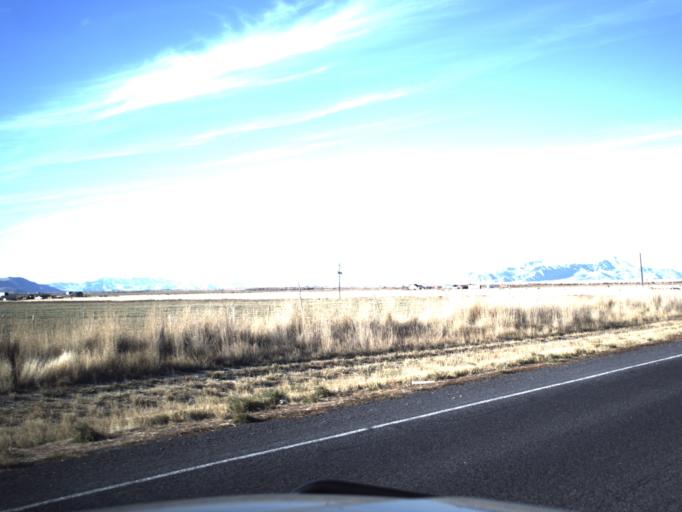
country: US
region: Utah
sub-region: Tooele County
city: Erda
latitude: 40.6027
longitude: -112.3707
